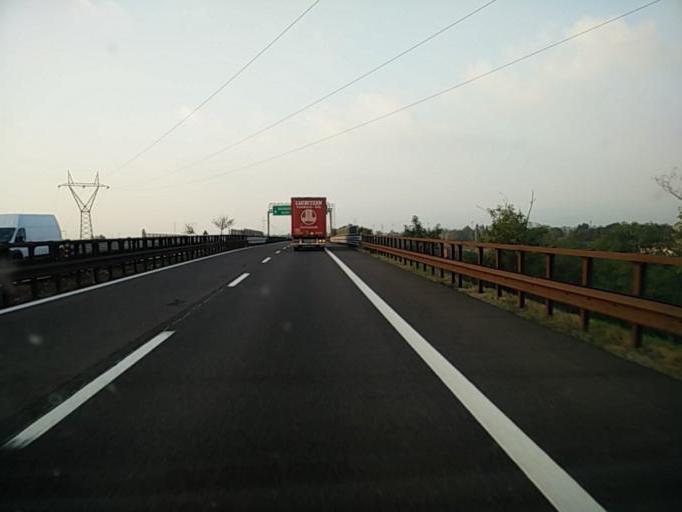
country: IT
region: Veneto
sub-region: Provincia di Verona
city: Caselle
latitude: 45.4265
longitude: 10.9100
